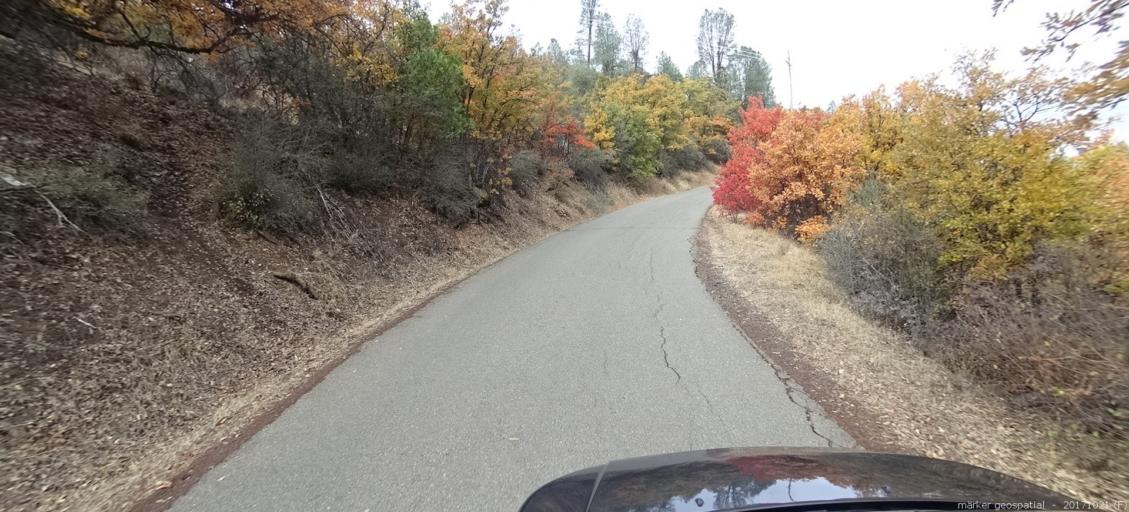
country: US
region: California
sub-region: Shasta County
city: Burney
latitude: 40.9590
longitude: -121.5530
